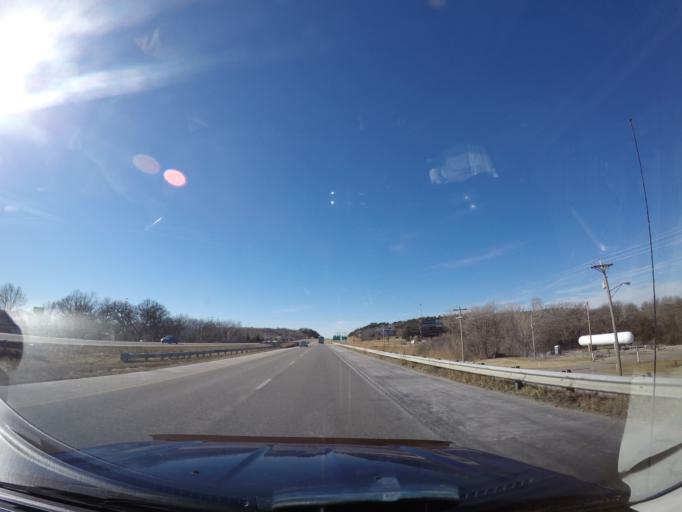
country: US
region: Kansas
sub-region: Geary County
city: Grandview Plaza
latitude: 39.0302
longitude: -96.7849
